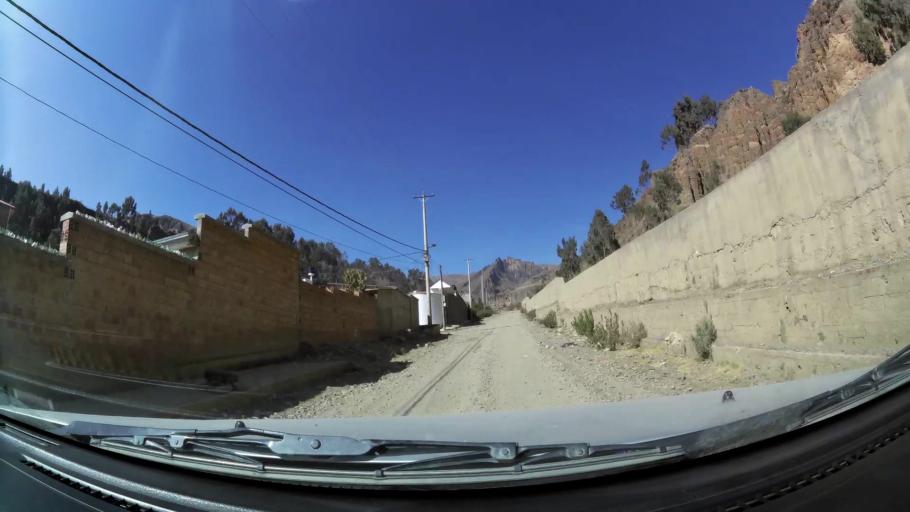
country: BO
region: La Paz
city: La Paz
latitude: -16.5099
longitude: -68.0426
